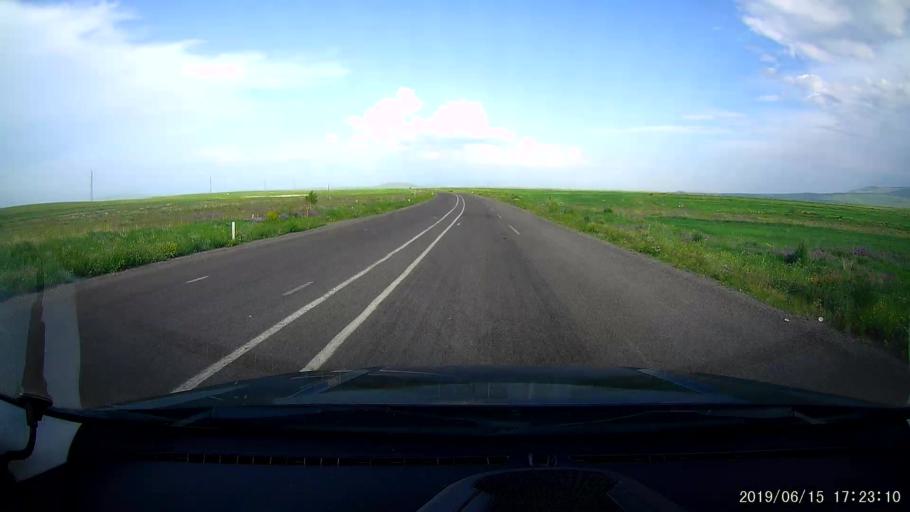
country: TR
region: Kars
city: Basgedikler
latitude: 40.6174
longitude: 43.3569
